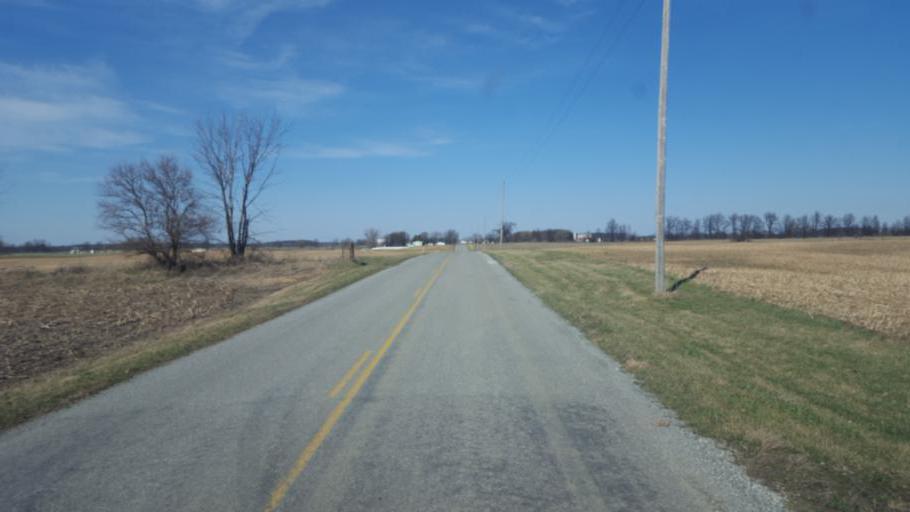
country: US
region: Ohio
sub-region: Union County
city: Richwood
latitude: 40.5264
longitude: -83.4344
